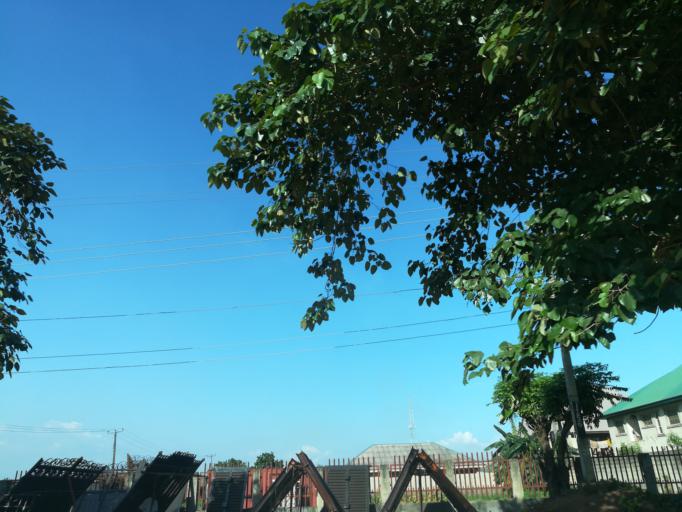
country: NG
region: Lagos
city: Ikorodu
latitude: 6.5737
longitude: 3.5288
